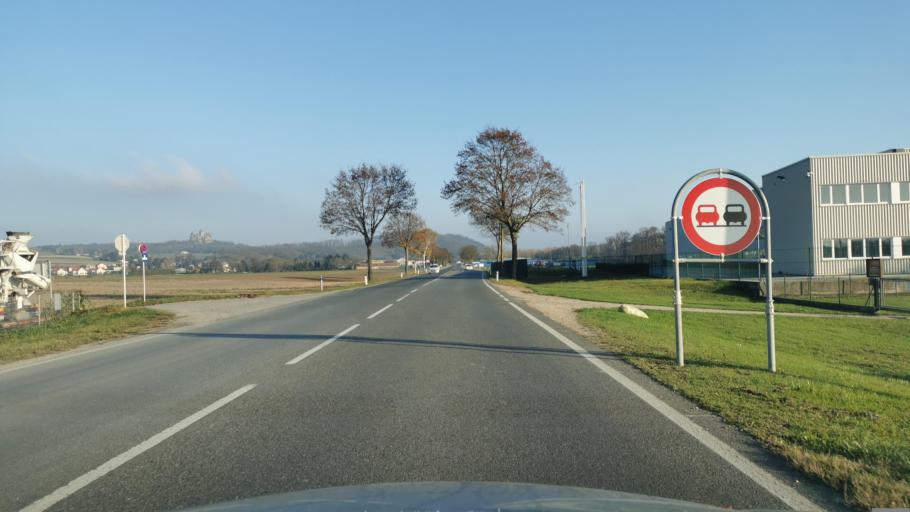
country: AT
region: Lower Austria
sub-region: Politischer Bezirk Korneuburg
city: Spillern
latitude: 48.3755
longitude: 16.2768
